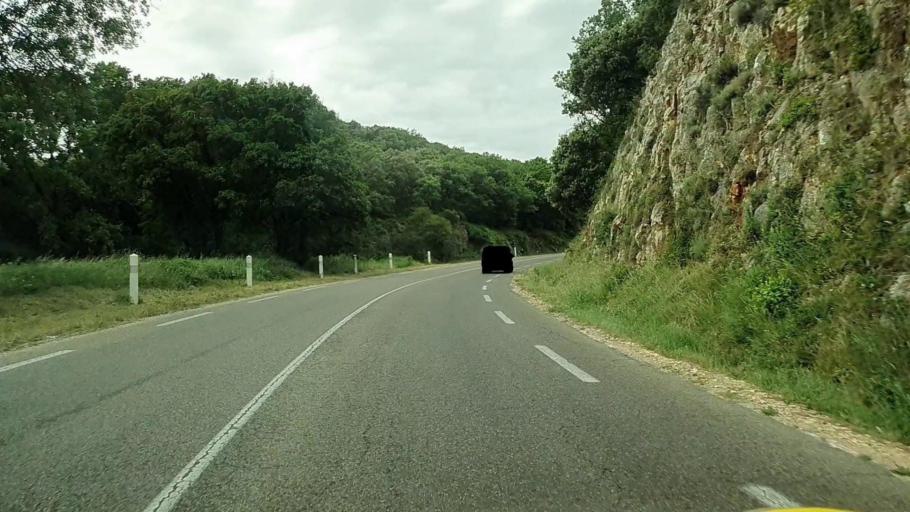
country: FR
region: Languedoc-Roussillon
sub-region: Departement du Gard
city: Connaux
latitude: 44.0632
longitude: 4.5751
